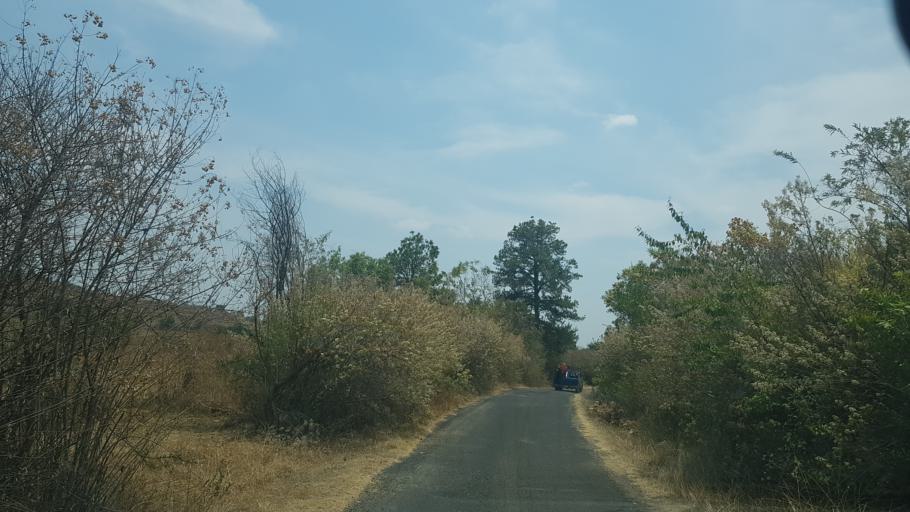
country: MX
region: Puebla
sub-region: Atzitzihuacan
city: Santiago Atzitzihuacan
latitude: 18.8504
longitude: -98.6110
